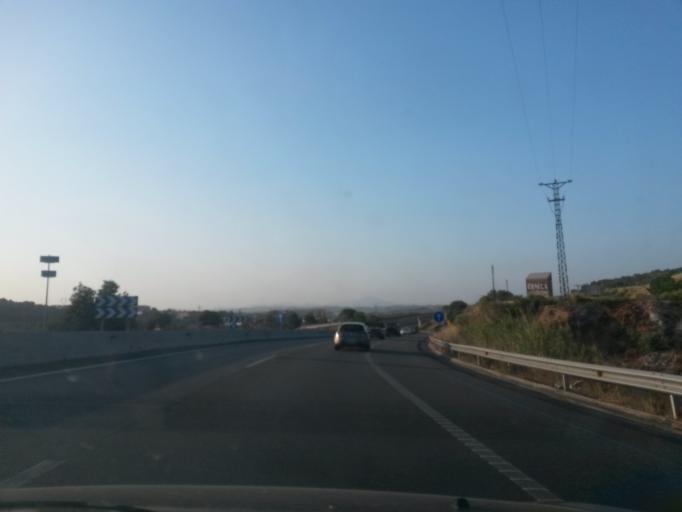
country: ES
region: Catalonia
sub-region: Provincia de Barcelona
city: Palleja
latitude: 41.4473
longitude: 1.9989
